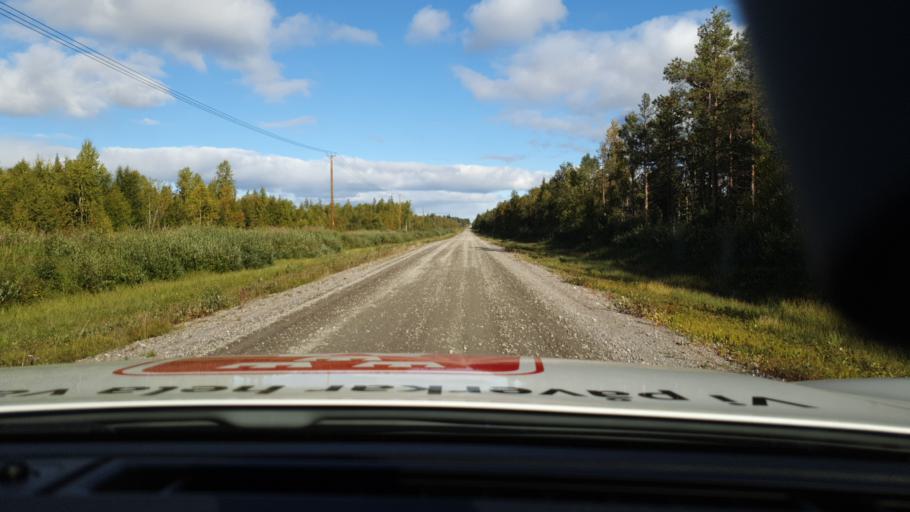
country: SE
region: Norrbotten
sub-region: Pajala Kommun
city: Pajala
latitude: 67.3814
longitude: 22.4039
